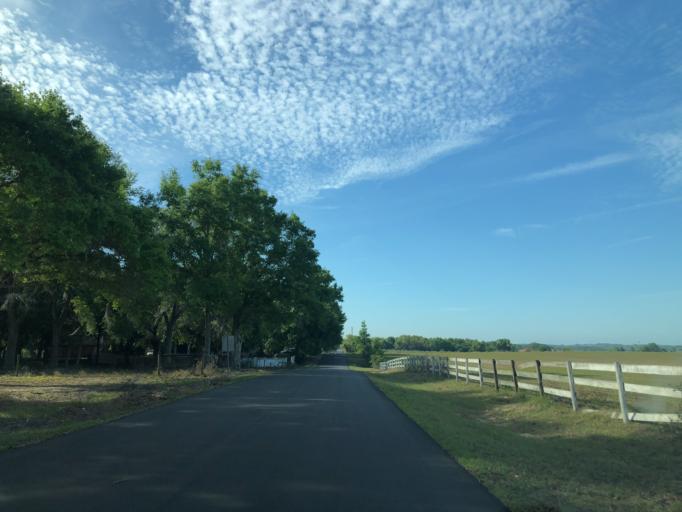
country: US
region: Florida
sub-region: Lake County
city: Astatula
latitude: 28.7183
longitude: -81.7413
